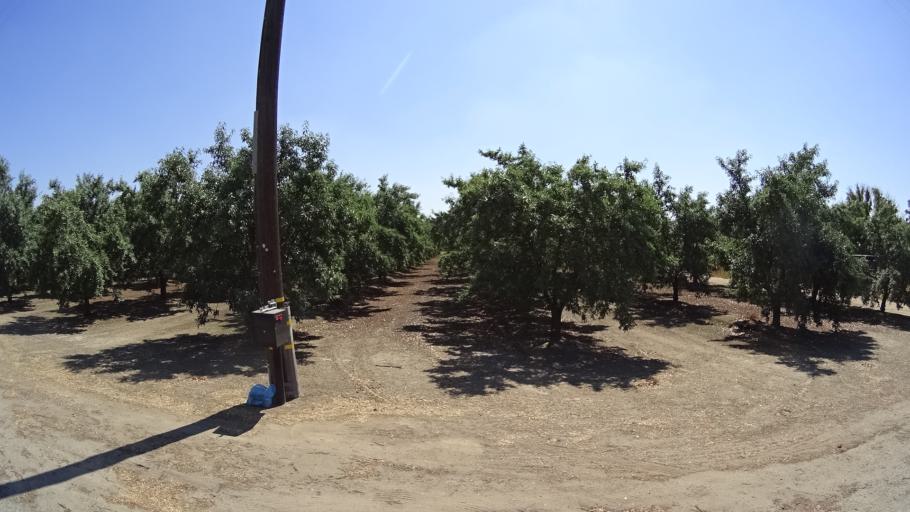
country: US
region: California
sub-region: Fresno County
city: Kingsburg
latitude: 36.4488
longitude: -119.5825
